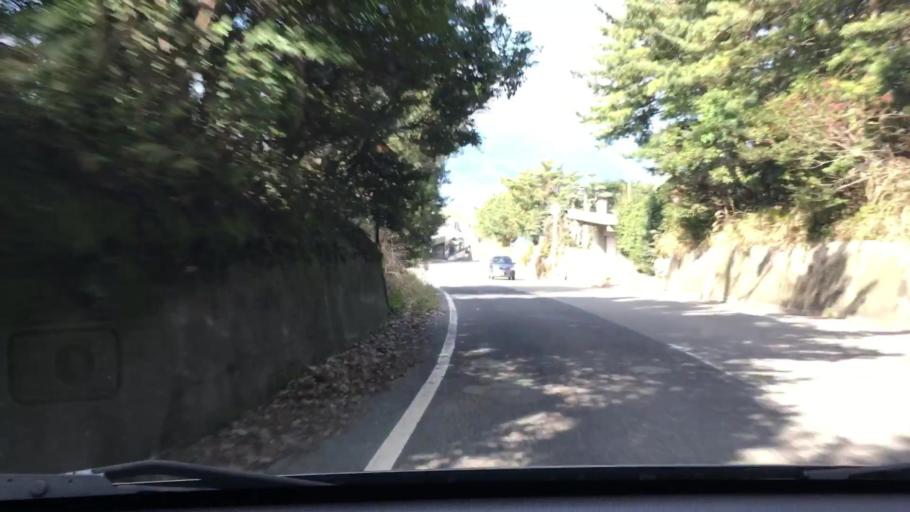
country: JP
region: Kagoshima
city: Kajiki
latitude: 31.6224
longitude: 130.6725
